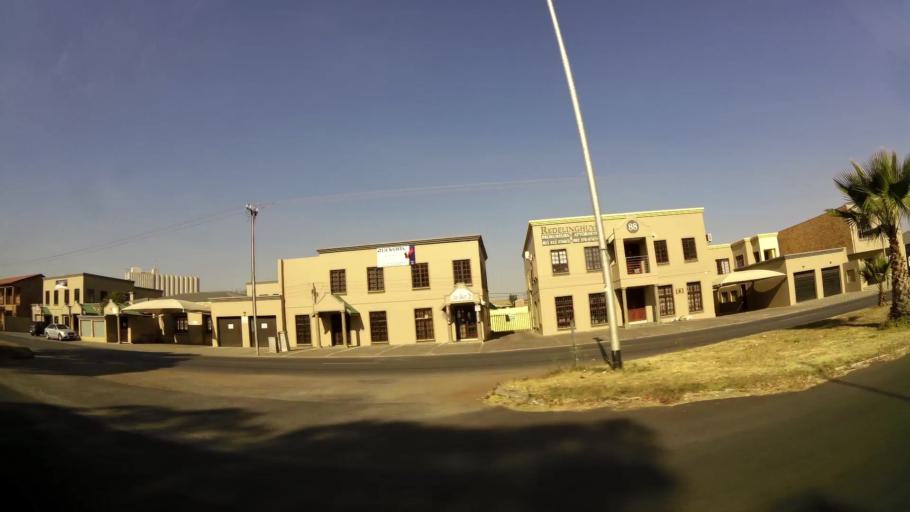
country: ZA
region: Gauteng
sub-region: West Rand District Municipality
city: Randfontein
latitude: -26.1657
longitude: 27.7069
